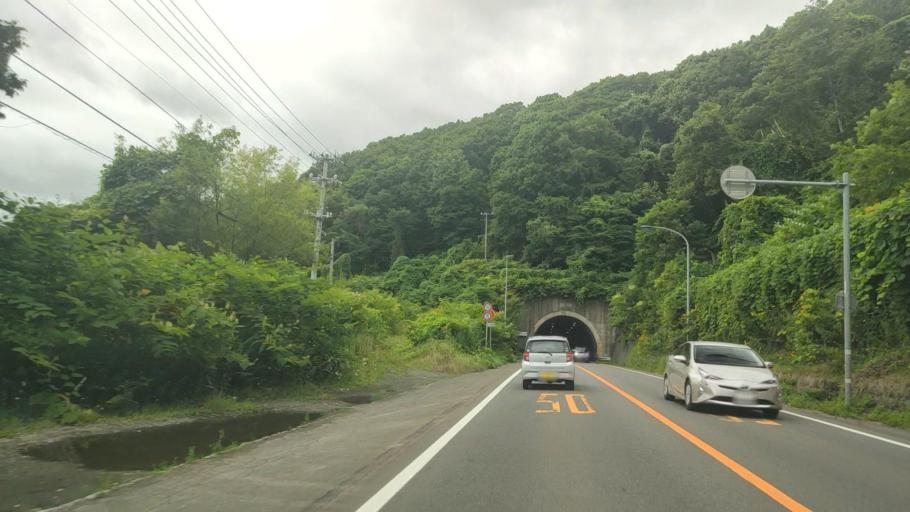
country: JP
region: Hokkaido
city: Date
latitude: 42.5699
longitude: 140.7343
